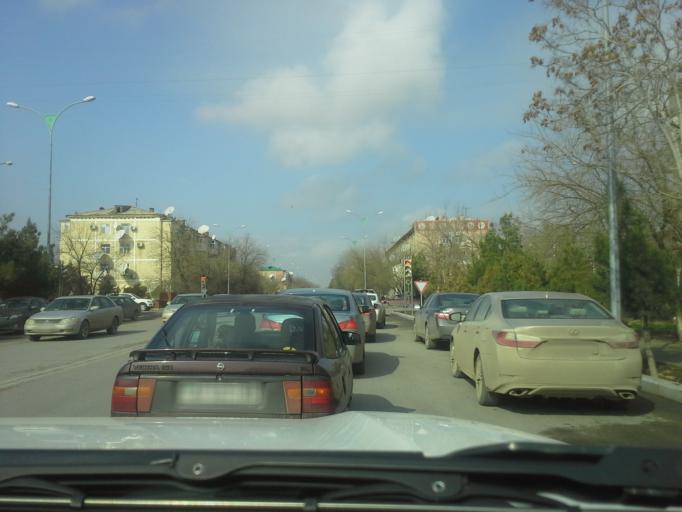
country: TM
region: Mary
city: Mary
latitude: 37.5933
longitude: 61.8295
